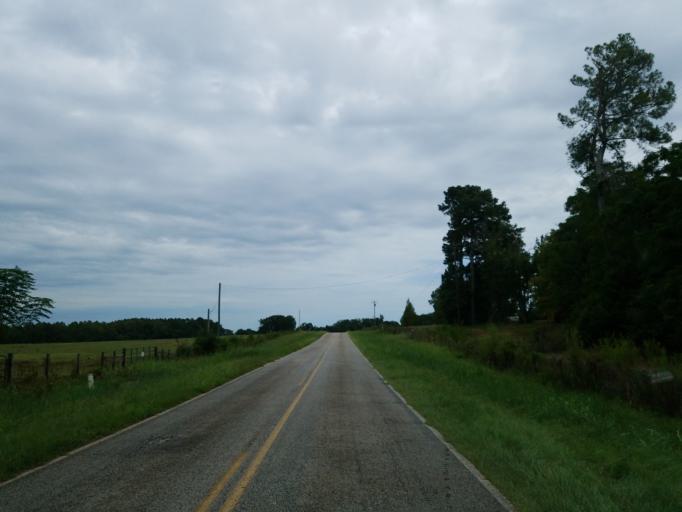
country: US
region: Georgia
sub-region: Monroe County
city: Forsyth
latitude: 32.9951
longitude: -84.0482
